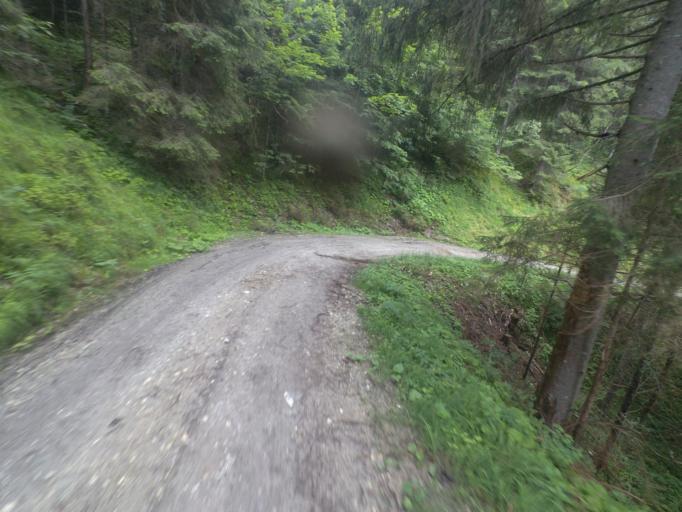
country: AT
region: Salzburg
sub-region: Politischer Bezirk Sankt Johann im Pongau
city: Schwarzach im Pongau
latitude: 47.3093
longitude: 13.1581
